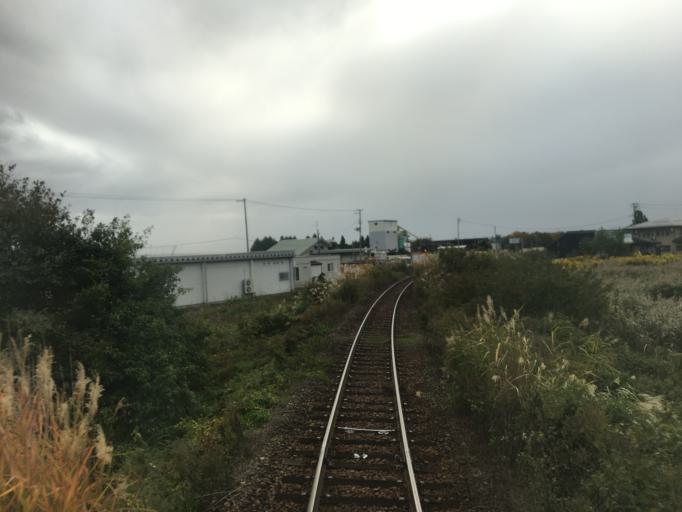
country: JP
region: Yamagata
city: Nagai
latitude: 38.0533
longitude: 140.0920
